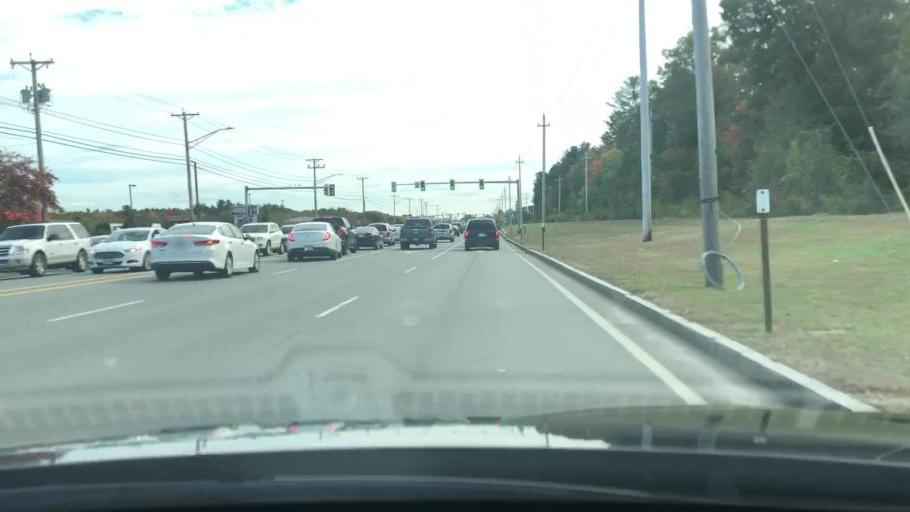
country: US
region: New Hampshire
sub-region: Rockingham County
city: Salem
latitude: 42.7635
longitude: -71.2162
